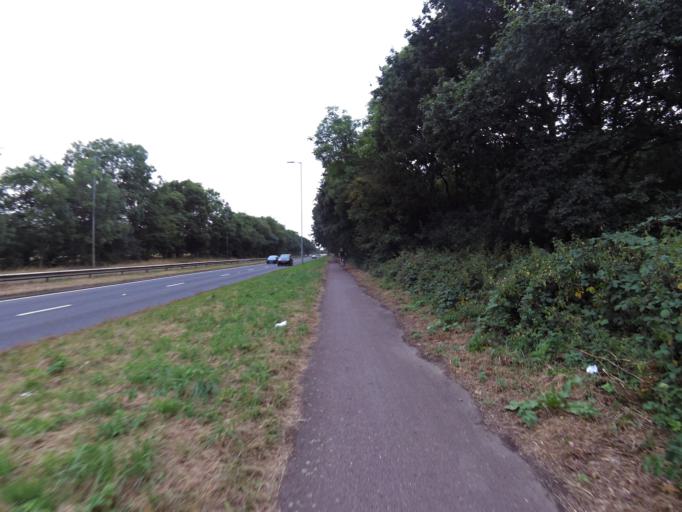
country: GB
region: England
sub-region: Hertfordshire
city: Shenley AV
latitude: 51.7357
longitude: -0.2824
